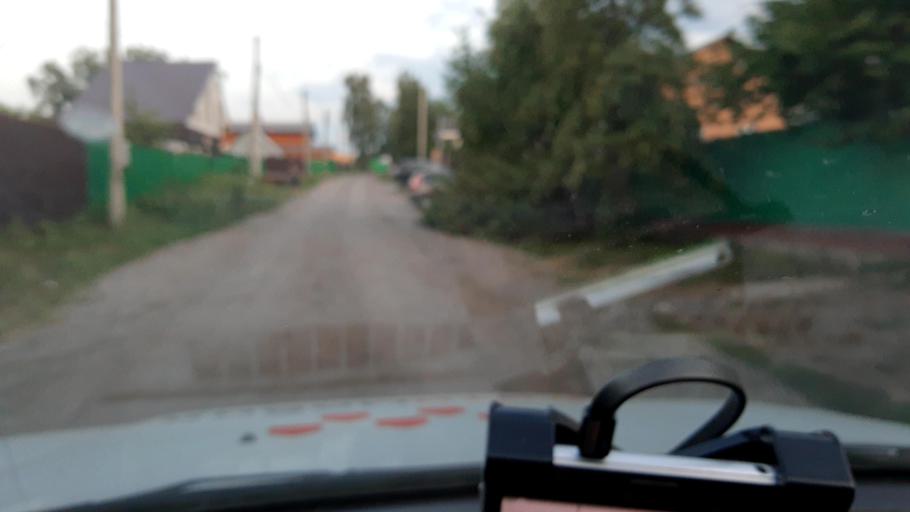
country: RU
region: Bashkortostan
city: Mikhaylovka
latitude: 54.8646
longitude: 55.8118
